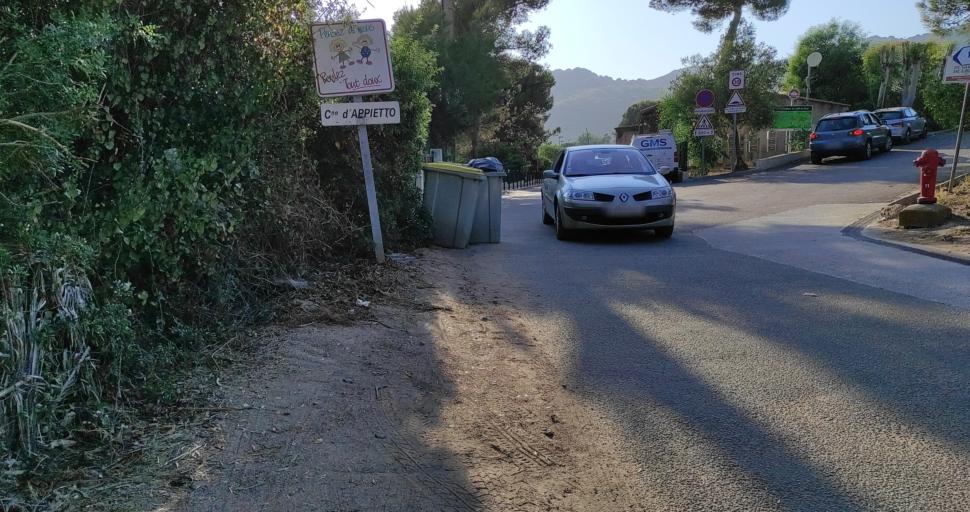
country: FR
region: Corsica
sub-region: Departement de la Corse-du-Sud
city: Alata
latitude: 41.9922
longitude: 8.6725
